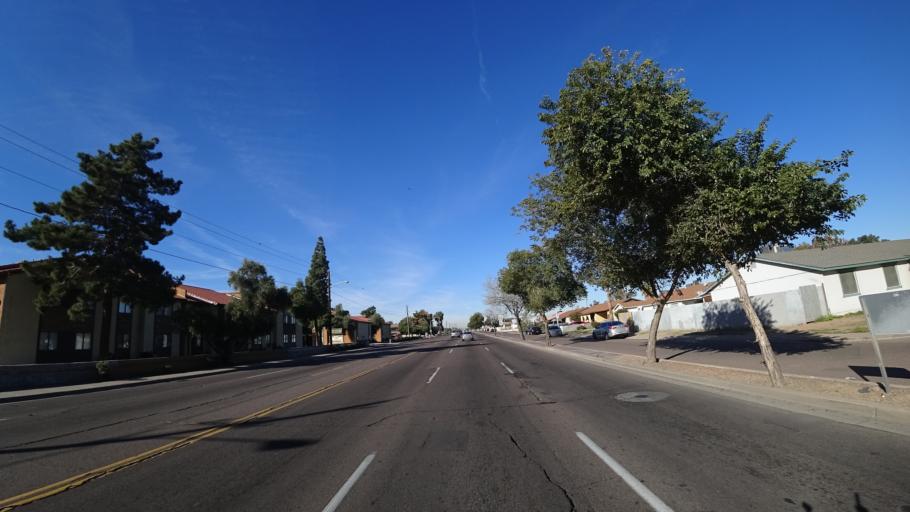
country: US
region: Arizona
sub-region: Maricopa County
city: Glendale
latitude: 33.4660
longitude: -112.1785
